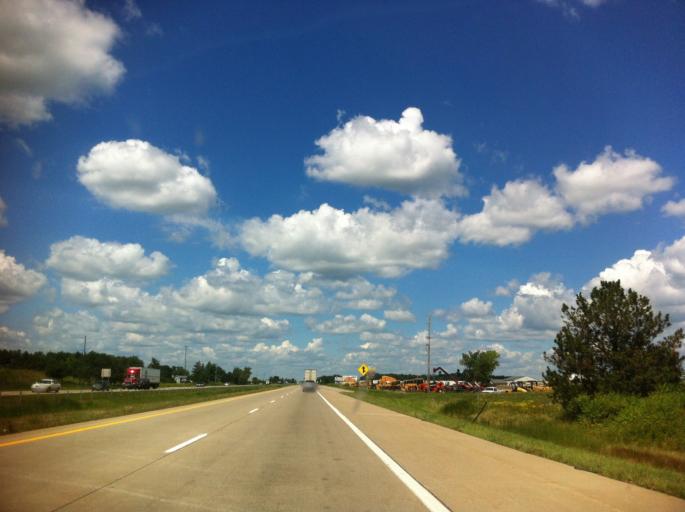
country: US
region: Ohio
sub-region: Lucas County
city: Sylvania
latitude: 41.7480
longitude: -83.6939
